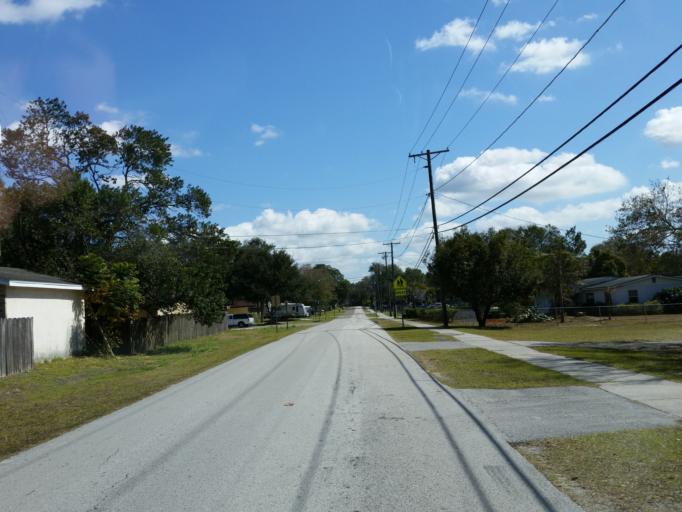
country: US
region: Florida
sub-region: Hillsborough County
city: Brandon
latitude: 27.9524
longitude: -82.2831
